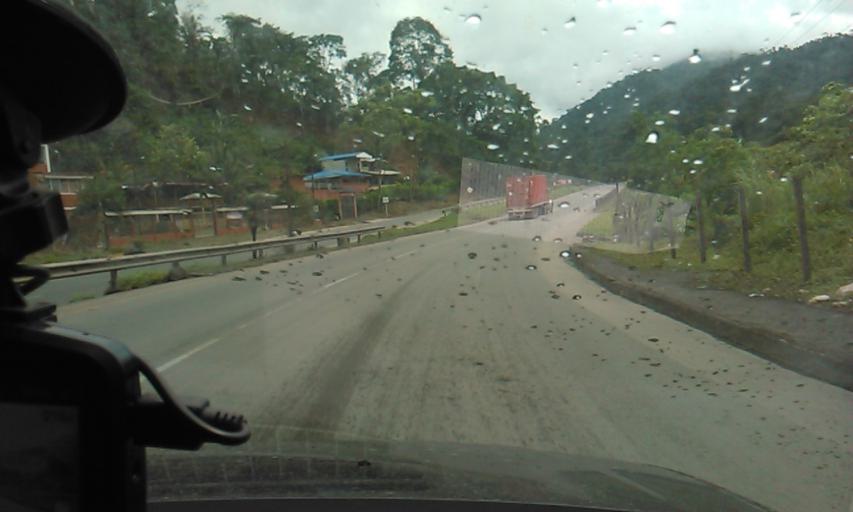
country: CO
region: Valle del Cauca
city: Dagua
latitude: 3.8513
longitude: -76.7988
